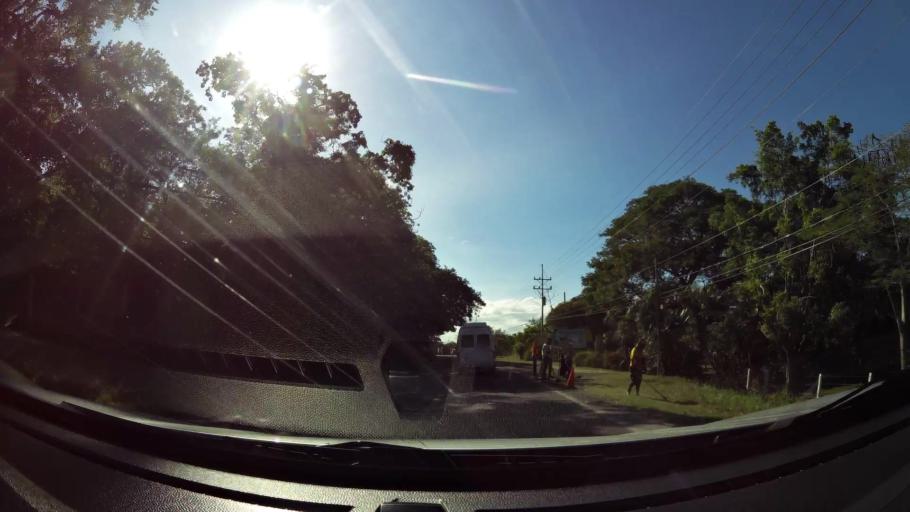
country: CR
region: Guanacaste
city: Sardinal
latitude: 10.5805
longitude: -85.5730
